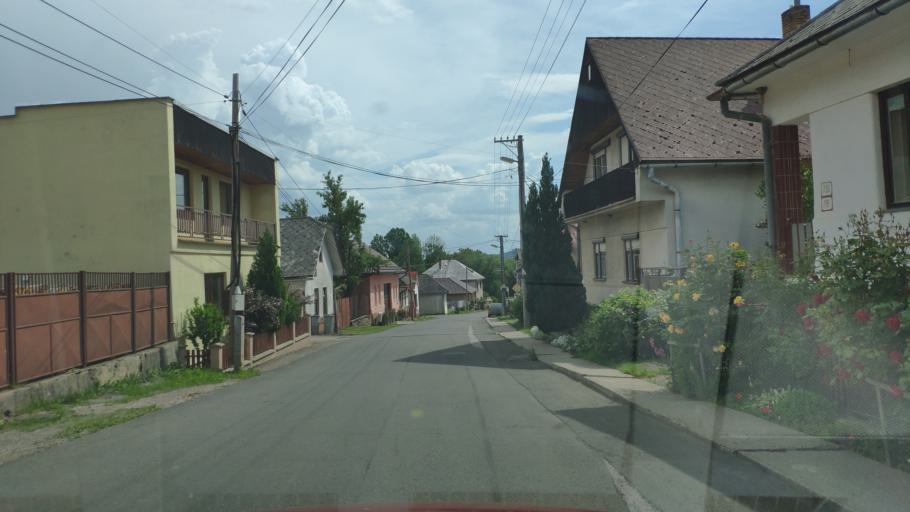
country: SK
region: Kosicky
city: Medzev
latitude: 48.7096
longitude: 20.9743
